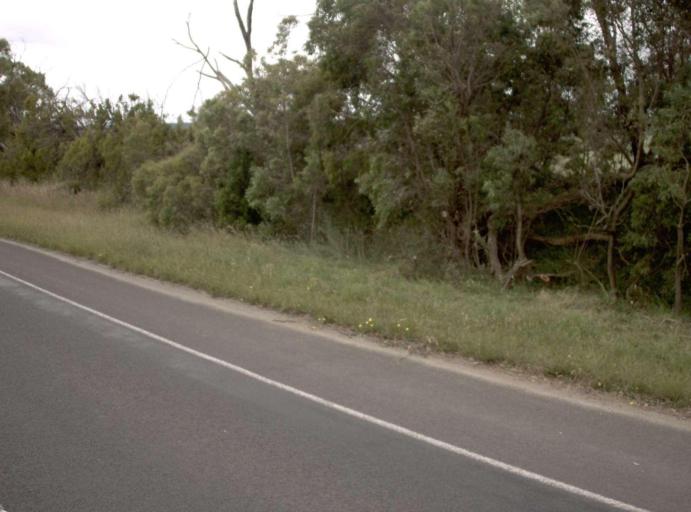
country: AU
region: Victoria
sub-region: Cardinia
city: Koo-Wee-Rup
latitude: -38.3050
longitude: 145.5703
